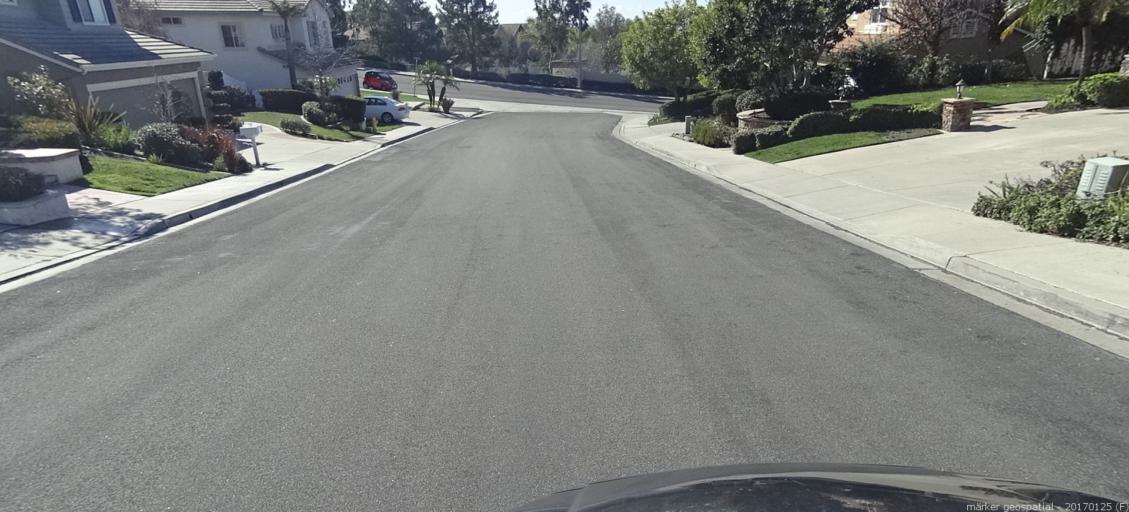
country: US
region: California
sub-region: Orange County
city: Foothill Ranch
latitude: 33.6875
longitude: -117.6561
